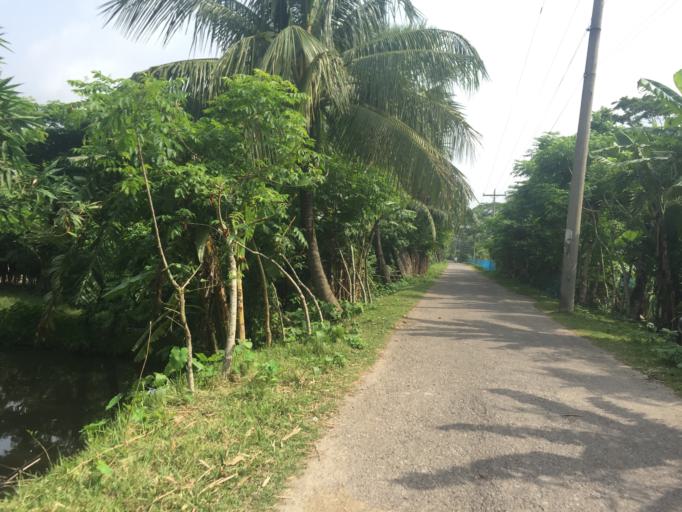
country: BD
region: Barisal
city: Mathba
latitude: 22.2342
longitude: 89.9155
